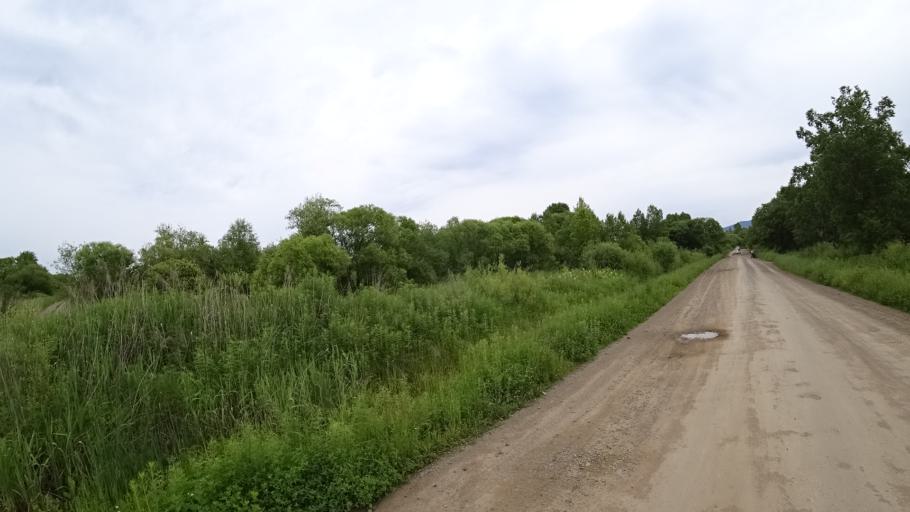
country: RU
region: Primorskiy
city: Arsen'yev
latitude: 44.1944
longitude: 133.3094
